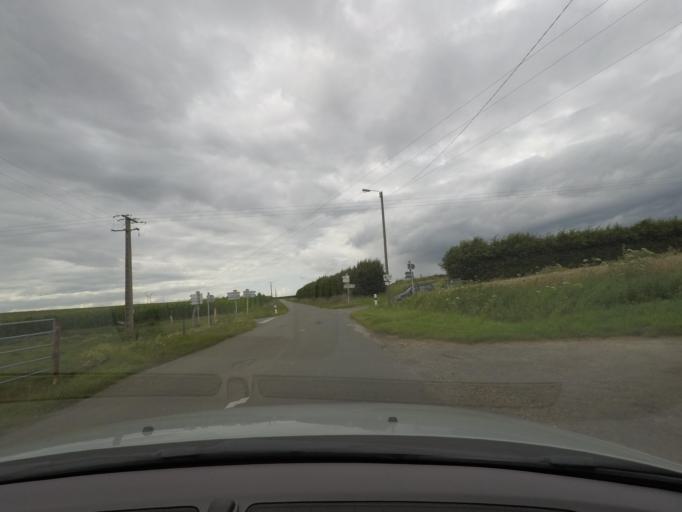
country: FR
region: Haute-Normandie
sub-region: Departement de l'Eure
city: Fleury-sur-Andelle
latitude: 49.2920
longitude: 1.3369
